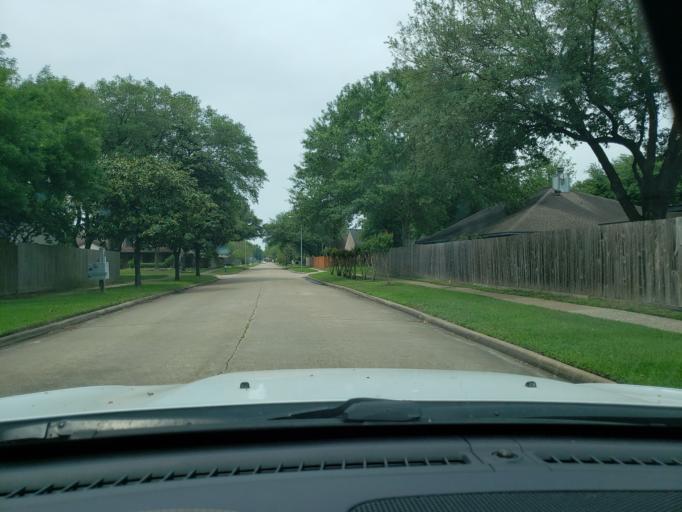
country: US
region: Texas
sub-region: Harris County
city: Jersey Village
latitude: 29.9157
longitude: -95.5735
